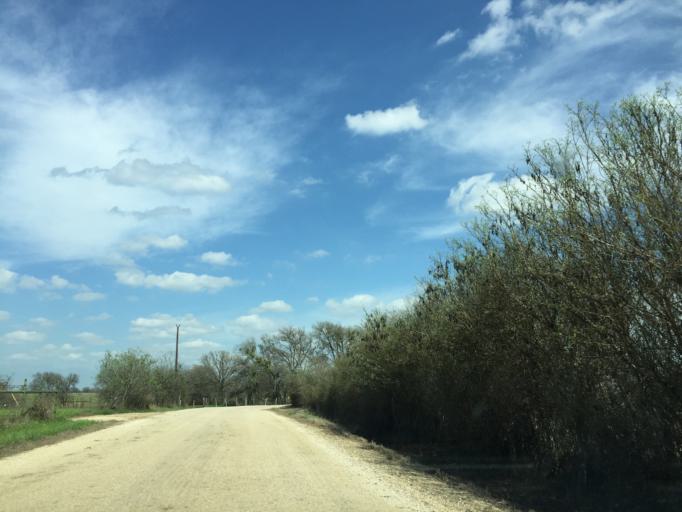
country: US
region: Texas
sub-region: Milam County
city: Thorndale
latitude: 30.5586
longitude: -97.2109
